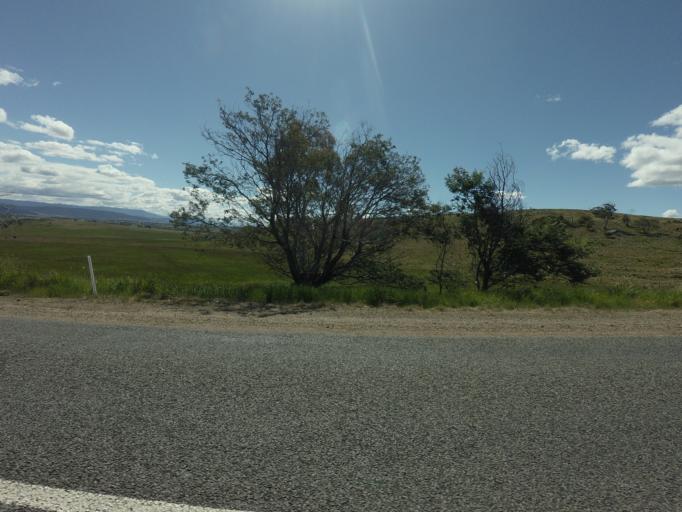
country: AU
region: Tasmania
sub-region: Northern Midlands
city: Evandale
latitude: -41.9369
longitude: 147.5723
